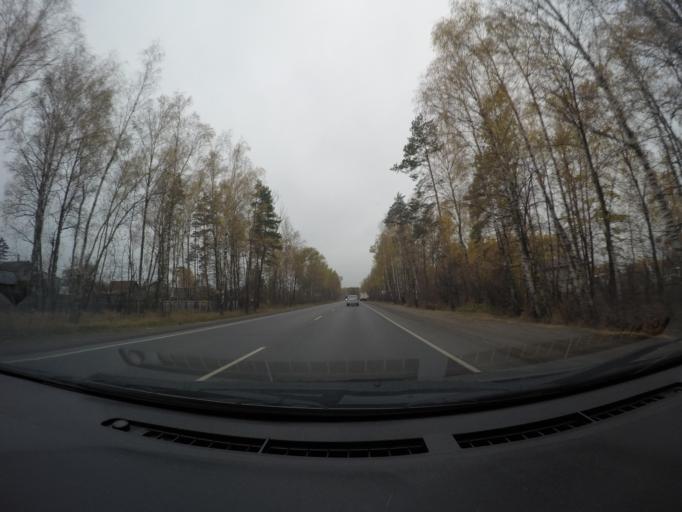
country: RU
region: Moskovskaya
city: Malyshevo
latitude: 55.4878
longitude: 38.3566
